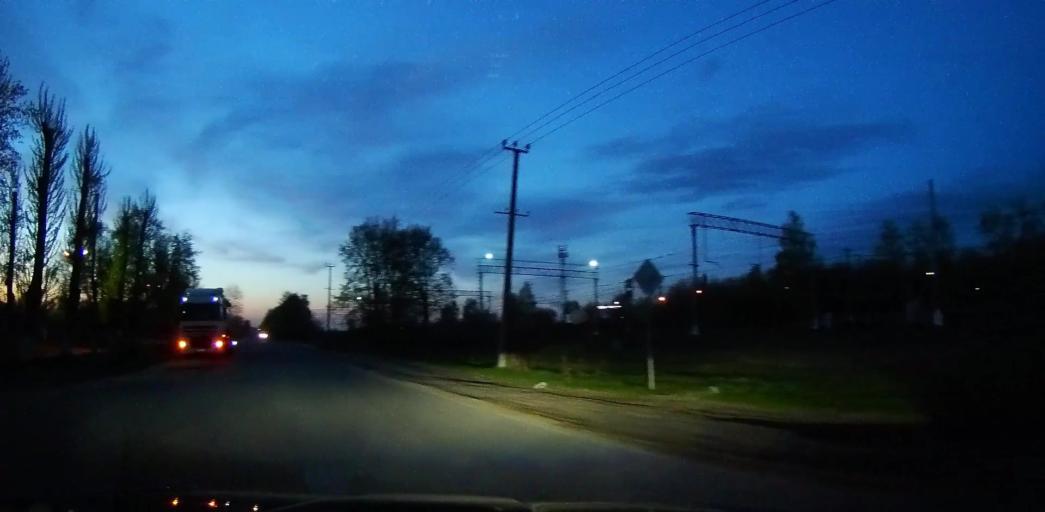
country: RU
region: Moskovskaya
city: Peski
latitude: 55.2094
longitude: 38.7726
